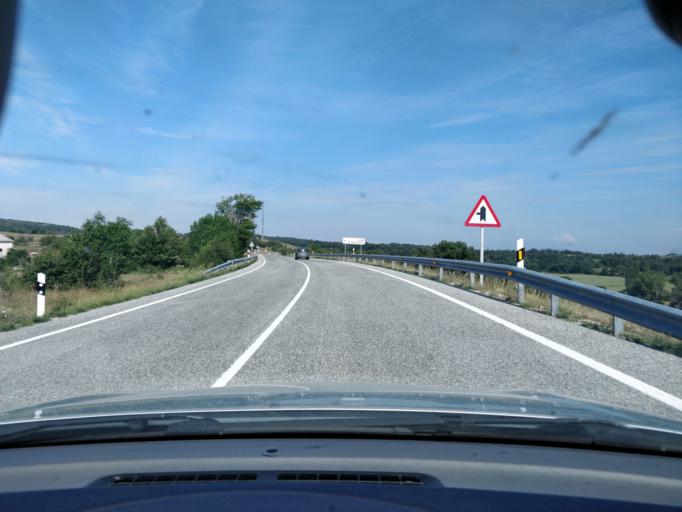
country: ES
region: Cantabria
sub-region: Provincia de Cantabria
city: San Martin de Elines
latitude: 42.9359
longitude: -3.7221
